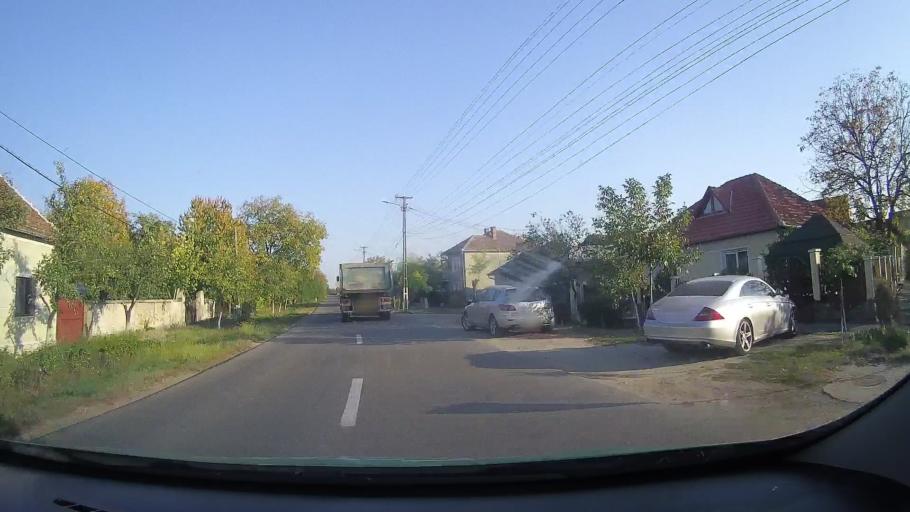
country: RO
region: Arad
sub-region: Comuna Pancota
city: Pancota
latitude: 46.3183
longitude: 21.6953
